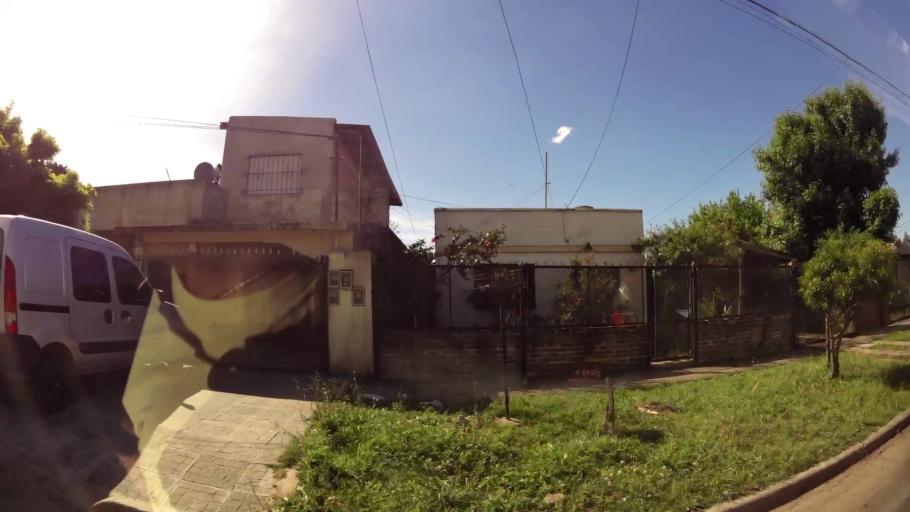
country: AR
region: Buenos Aires
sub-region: Partido de Almirante Brown
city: Adrogue
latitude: -34.8035
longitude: -58.3619
